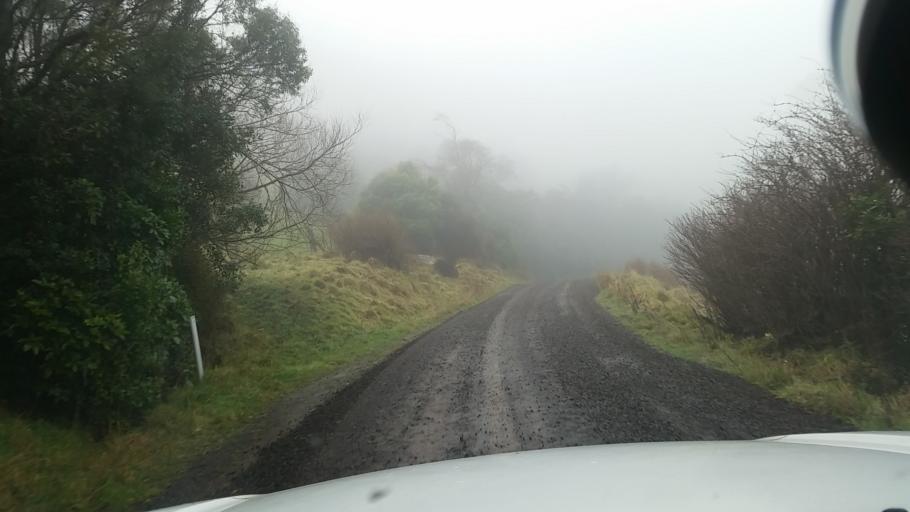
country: NZ
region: Canterbury
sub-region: Christchurch City
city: Christchurch
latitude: -43.7411
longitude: 172.9017
